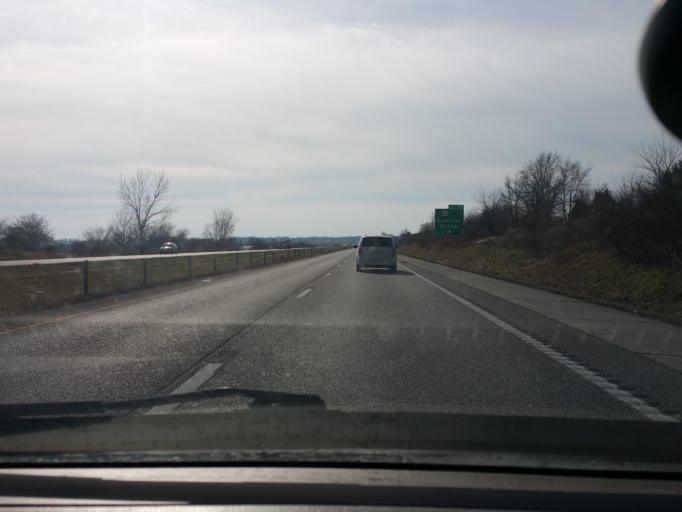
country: US
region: Missouri
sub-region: Clay County
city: Liberty
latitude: 39.2937
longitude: -94.4123
